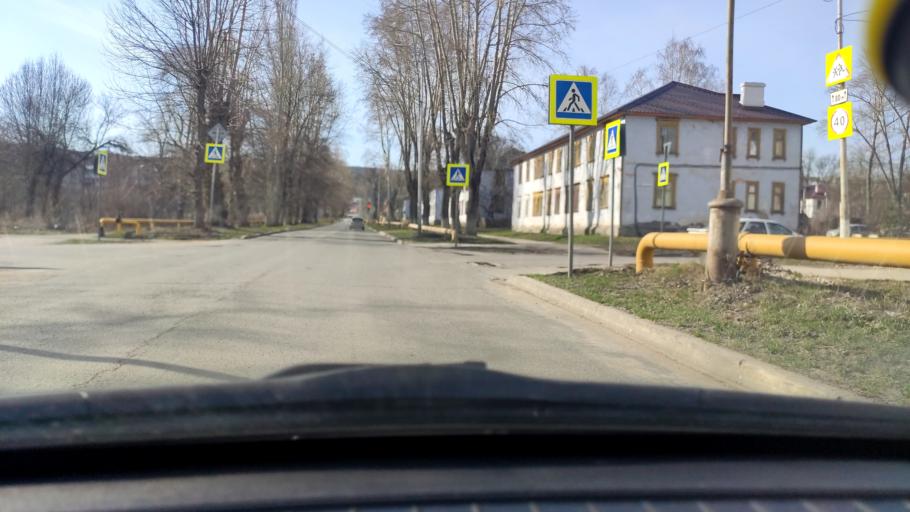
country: RU
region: Samara
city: Zhigulevsk
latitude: 53.3994
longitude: 49.4976
